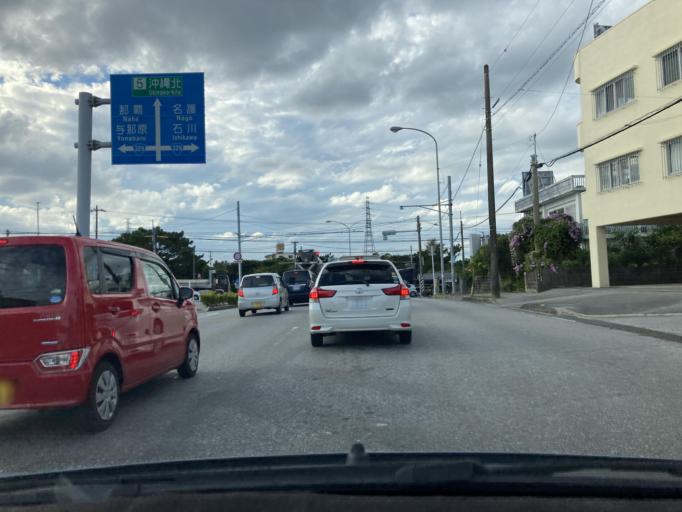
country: JP
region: Okinawa
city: Okinawa
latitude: 26.3746
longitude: 127.8218
